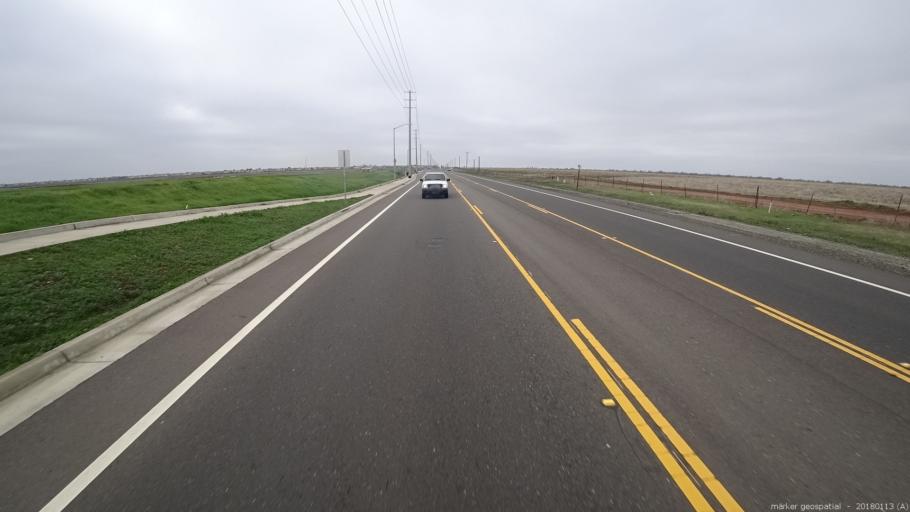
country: US
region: California
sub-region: Sacramento County
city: Gold River
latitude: 38.5592
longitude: -121.2220
